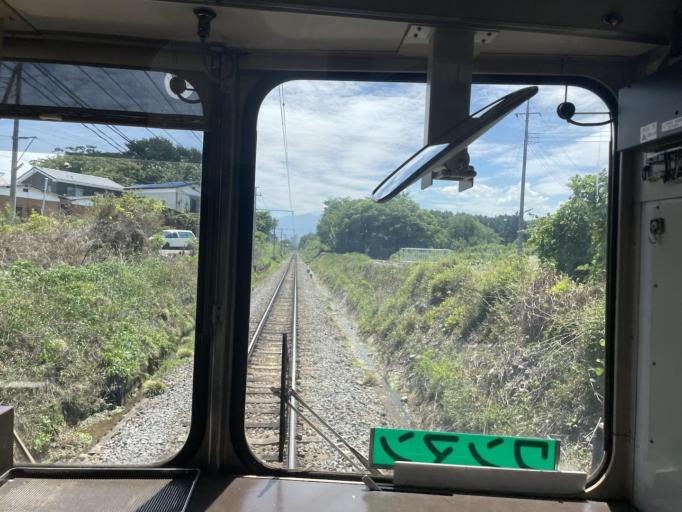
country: JP
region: Saitama
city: Chichibu
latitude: 36.0419
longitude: 139.1002
